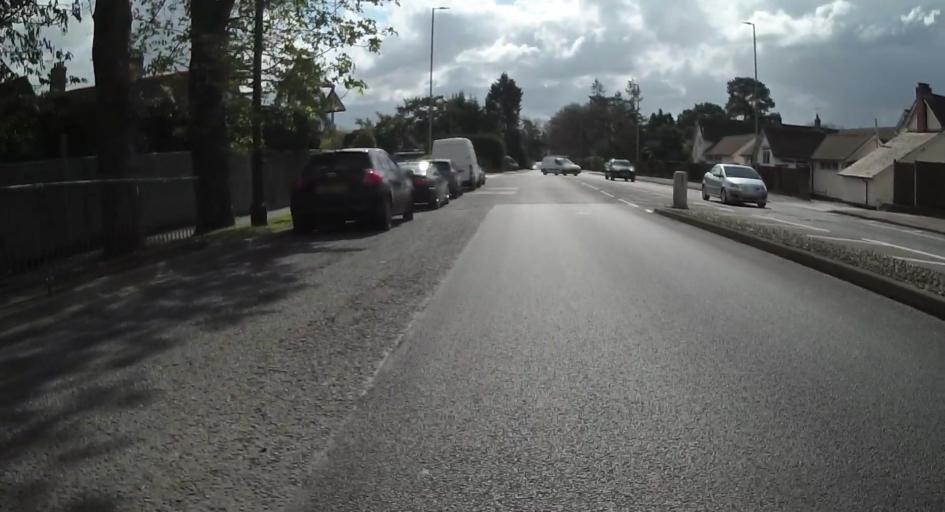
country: GB
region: England
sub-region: Surrey
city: West Byfleet
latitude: 51.3365
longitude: -0.5124
